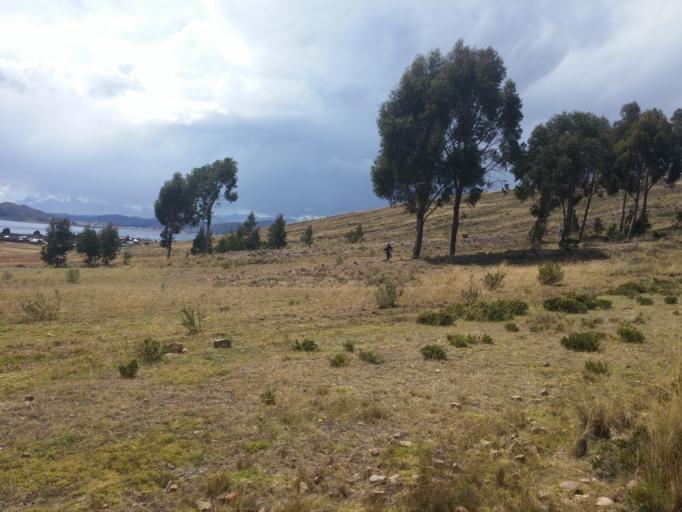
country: BO
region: La Paz
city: Batallas
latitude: -16.2937
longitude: -68.5977
